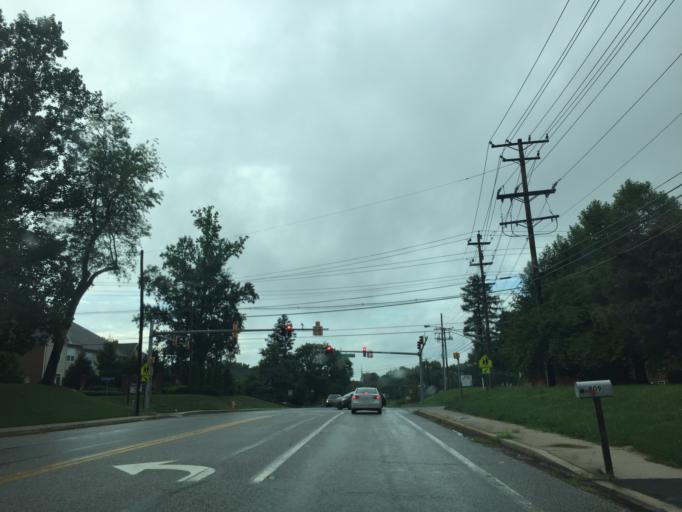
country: US
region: Maryland
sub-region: Harford County
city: South Bel Air
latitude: 39.5262
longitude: -76.3395
